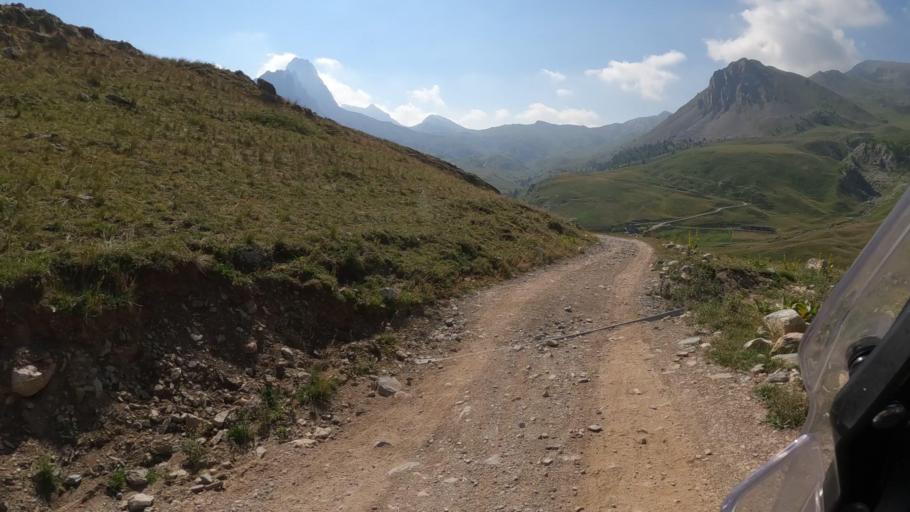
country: IT
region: Piedmont
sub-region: Provincia di Cuneo
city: Pietraporzio
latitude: 44.4028
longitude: 7.0359
